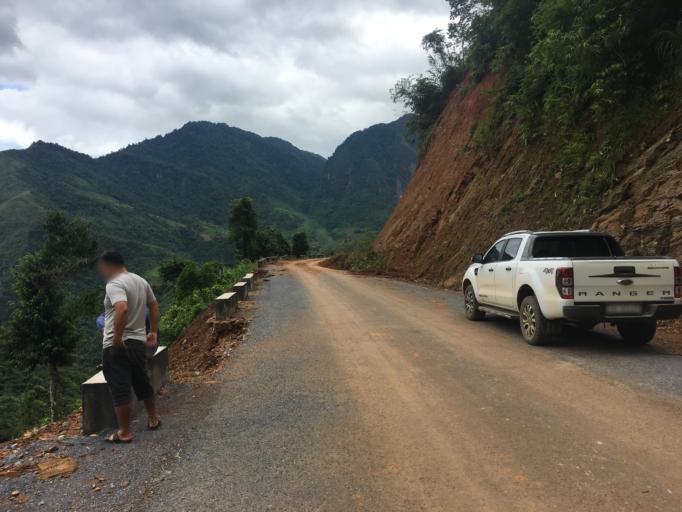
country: VN
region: Ha Giang
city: Thi Tran Tam Son
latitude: 22.9527
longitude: 105.0377
